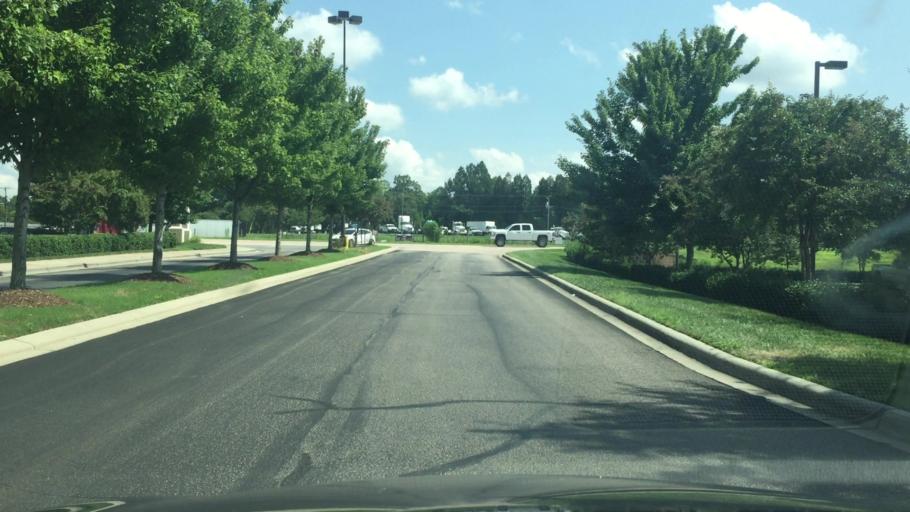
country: US
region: North Carolina
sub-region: Rowan County
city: Salisbury
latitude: 35.6374
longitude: -80.4886
